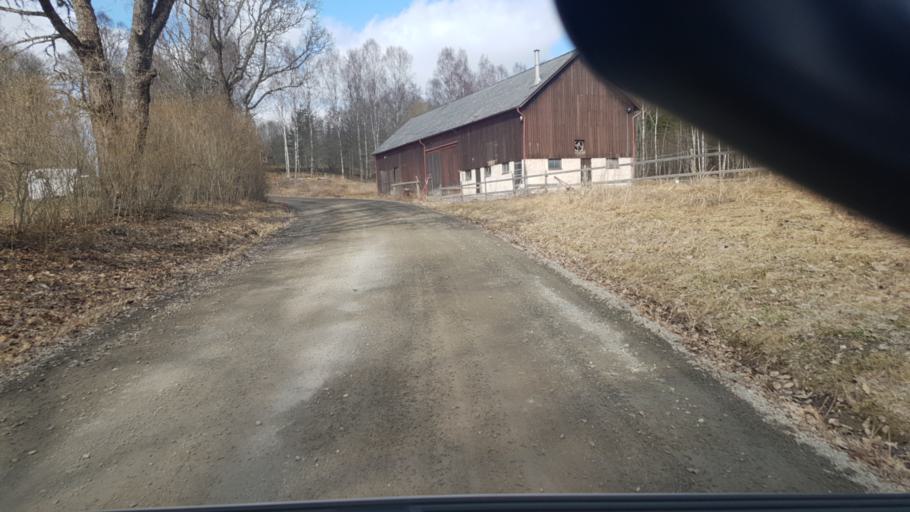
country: SE
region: Vaermland
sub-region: Eda Kommun
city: Amotfors
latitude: 59.7641
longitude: 12.4450
